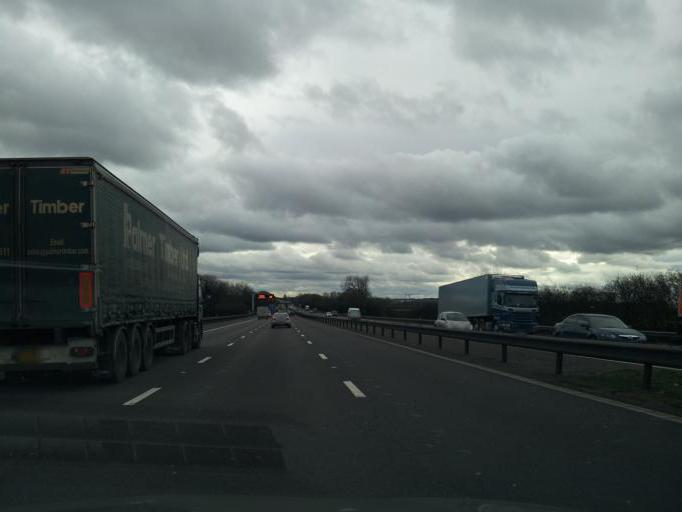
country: GB
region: England
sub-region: Staffordshire
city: Stone
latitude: 52.8587
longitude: -2.1625
